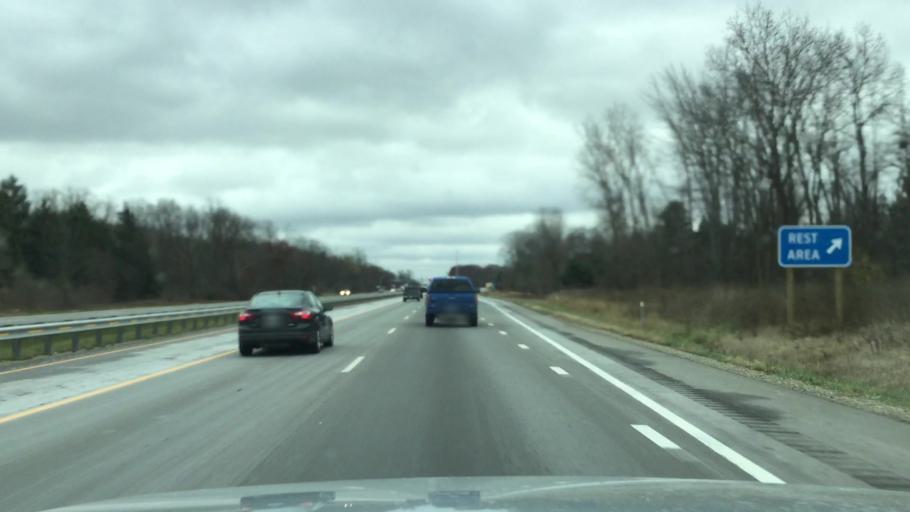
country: US
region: Michigan
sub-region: Livingston County
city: Whitmore Lake
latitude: 42.3611
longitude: -83.7496
